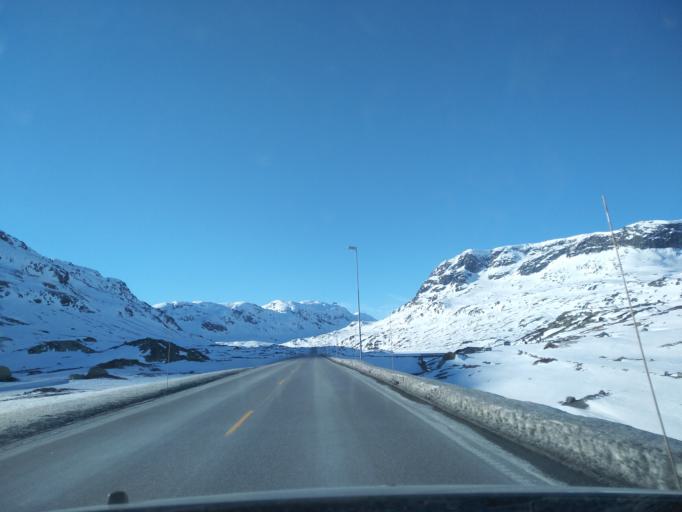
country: NO
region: Aust-Agder
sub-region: Bykle
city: Hovden
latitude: 59.8482
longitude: 7.1305
